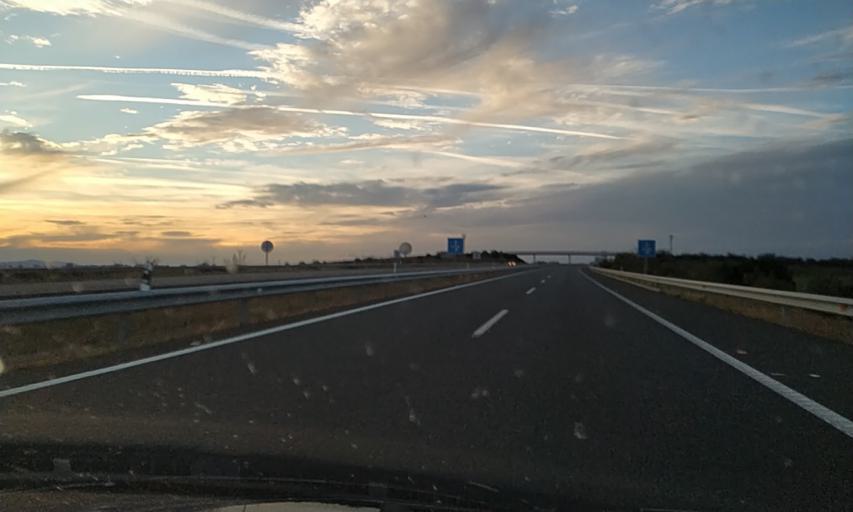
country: ES
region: Extremadura
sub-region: Provincia de Caceres
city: Aldea del Cano
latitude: 39.2815
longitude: -6.3268
